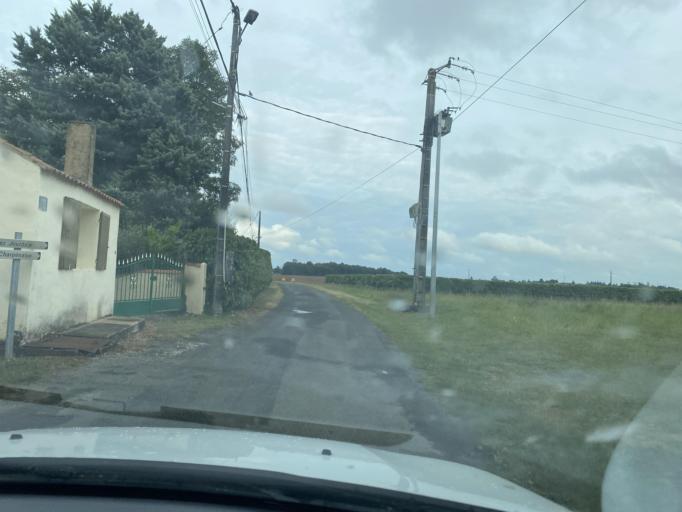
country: FR
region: Poitou-Charentes
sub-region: Departement de la Charente-Maritime
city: Gemozac
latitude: 45.5419
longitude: -0.6518
